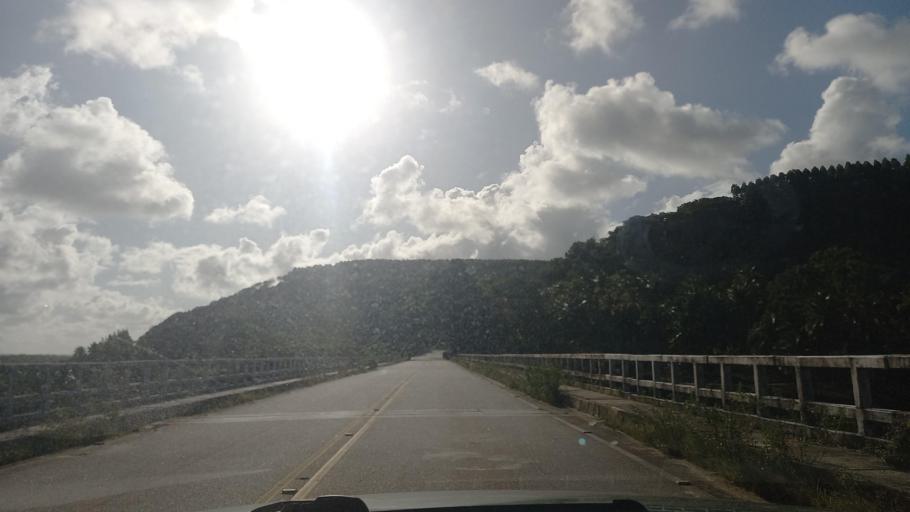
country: BR
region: Alagoas
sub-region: Marechal Deodoro
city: Marechal Deodoro
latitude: -9.8378
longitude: -35.9268
